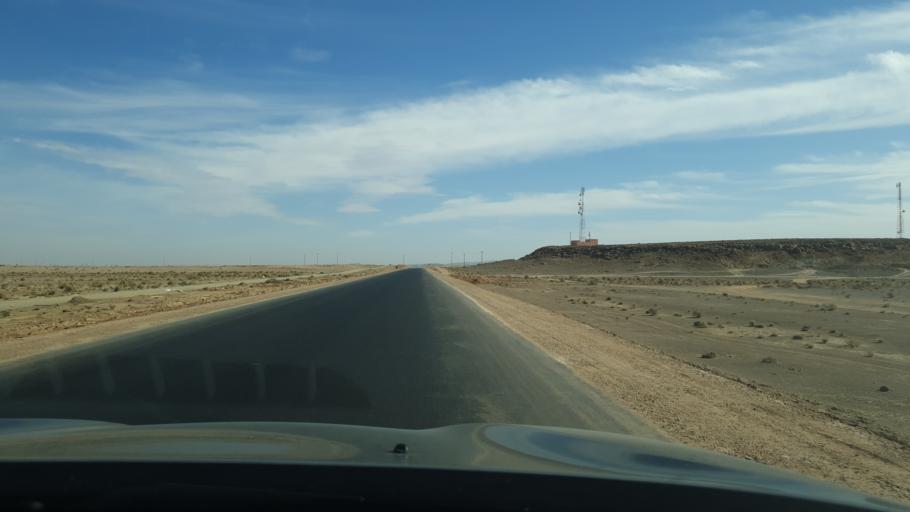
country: MA
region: Meknes-Tafilalet
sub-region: Errachidia
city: Goulmima
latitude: 31.4849
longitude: -5.1355
